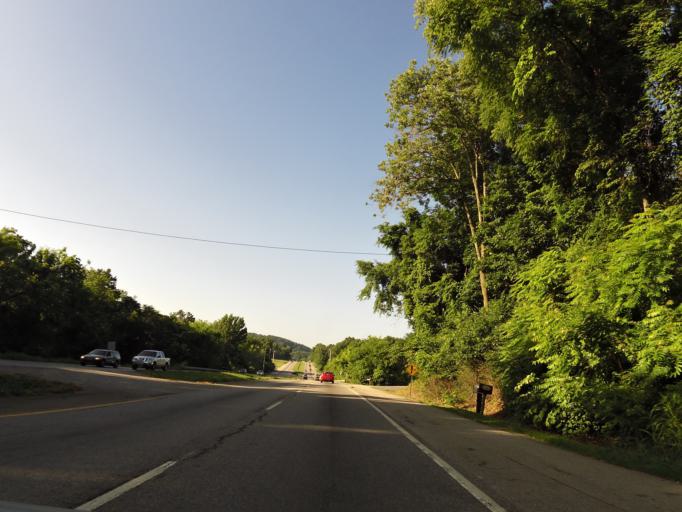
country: US
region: Tennessee
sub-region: Blount County
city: Eagleton Village
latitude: 35.8695
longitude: -83.9598
